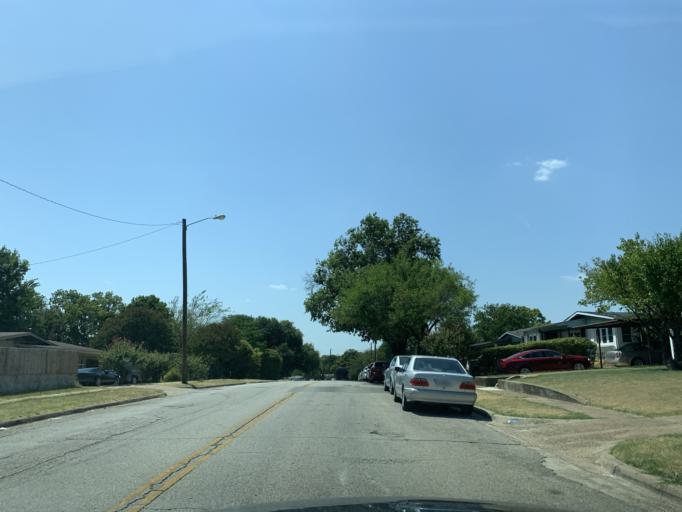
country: US
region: Texas
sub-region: Dallas County
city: Cockrell Hill
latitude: 32.6924
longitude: -96.8077
